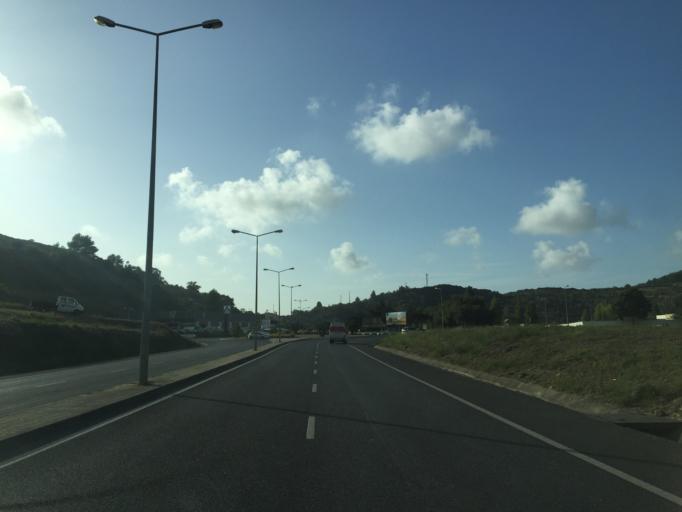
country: PT
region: Lisbon
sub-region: Torres Vedras
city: Torres Vedras
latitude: 39.0909
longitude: -9.2655
